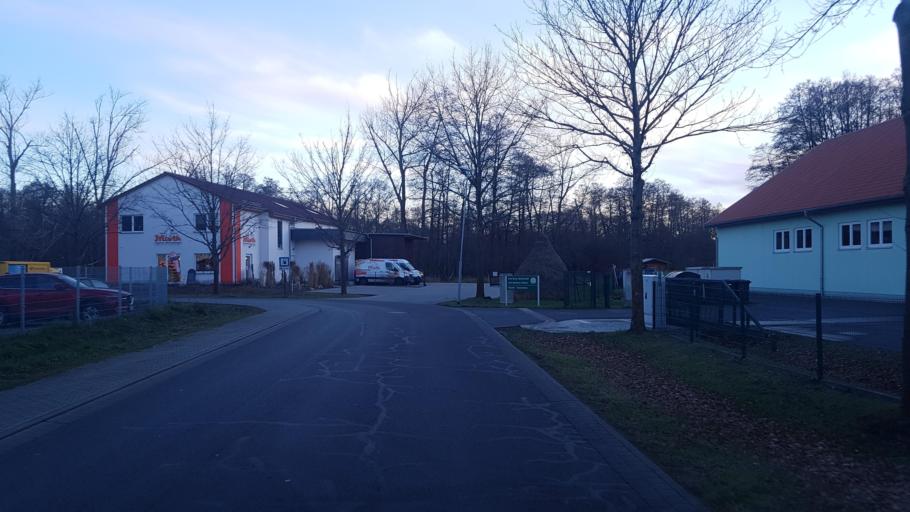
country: DE
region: Brandenburg
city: Burg
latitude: 51.8239
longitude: 14.1420
